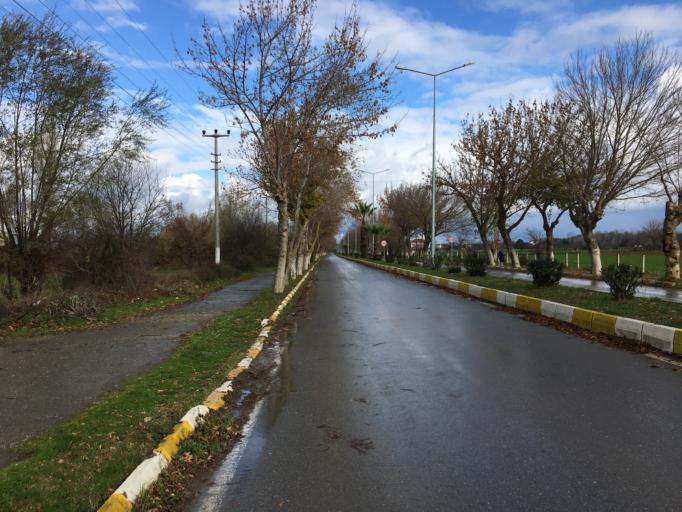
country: TR
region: Samsun
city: Alacam
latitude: 41.6231
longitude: 35.6081
